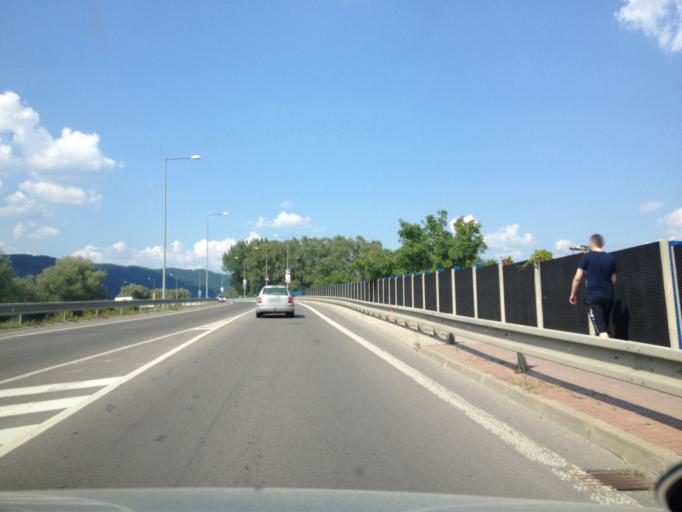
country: SK
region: Nitriansky
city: Puchov
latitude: 49.1112
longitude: 18.3157
